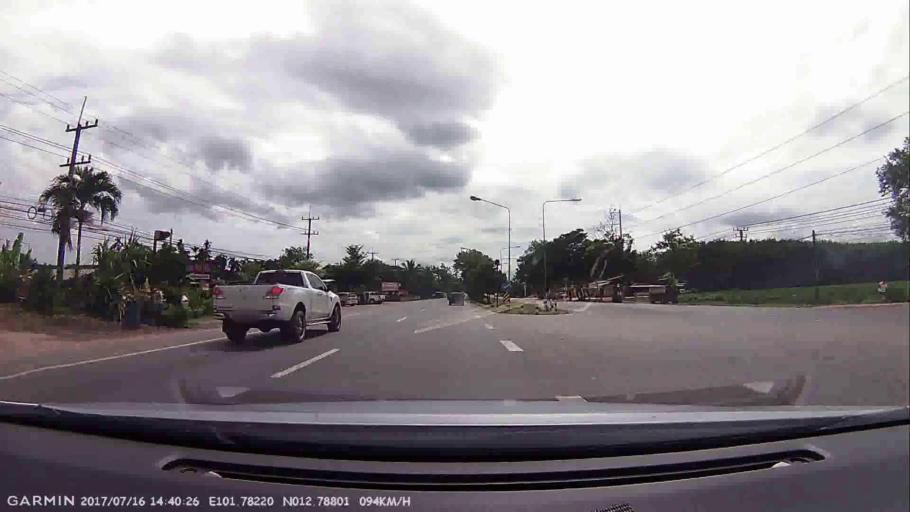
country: TH
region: Chanthaburi
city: Na Yai Am
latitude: 12.7880
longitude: 101.7820
